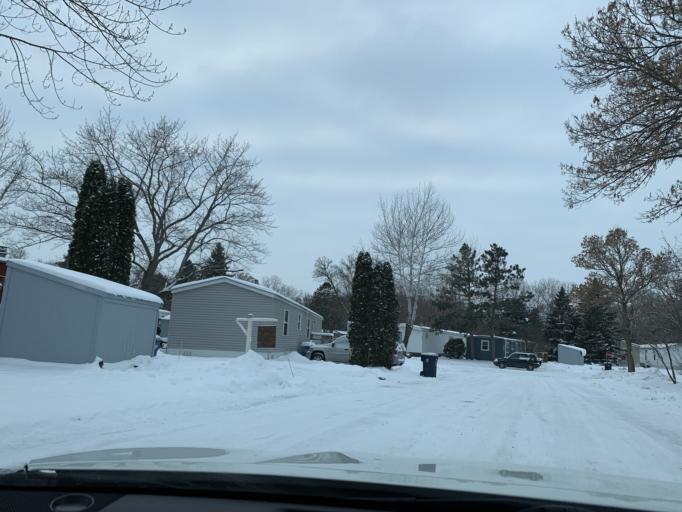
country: US
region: Minnesota
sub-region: Anoka County
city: Coon Rapids
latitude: 45.1570
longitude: -93.2946
